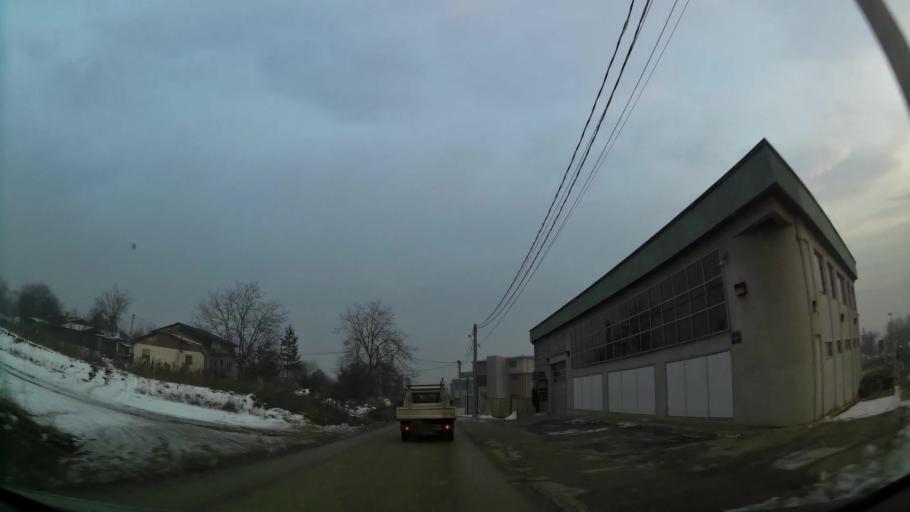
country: MK
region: Suto Orizari
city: Suto Orizare
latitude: 42.0292
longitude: 21.4078
